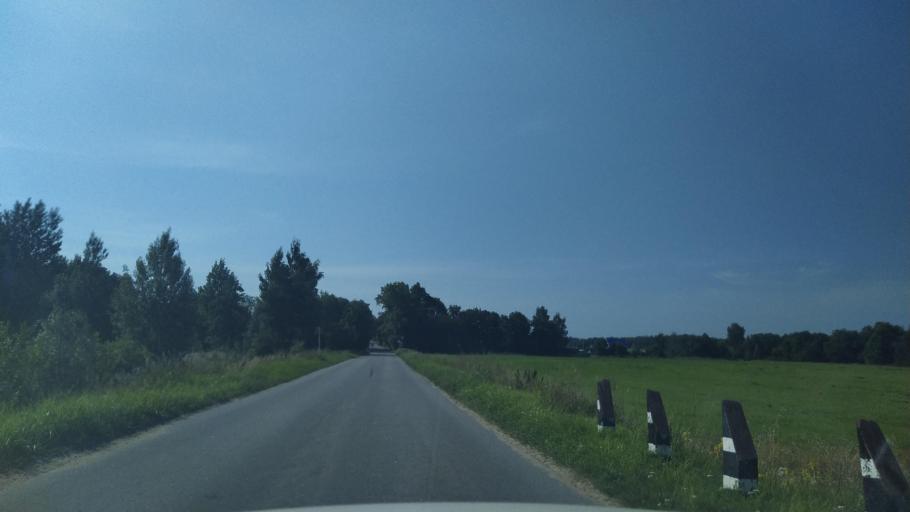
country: RU
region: Leningrad
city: Siverskiy
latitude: 59.2798
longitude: 30.0508
